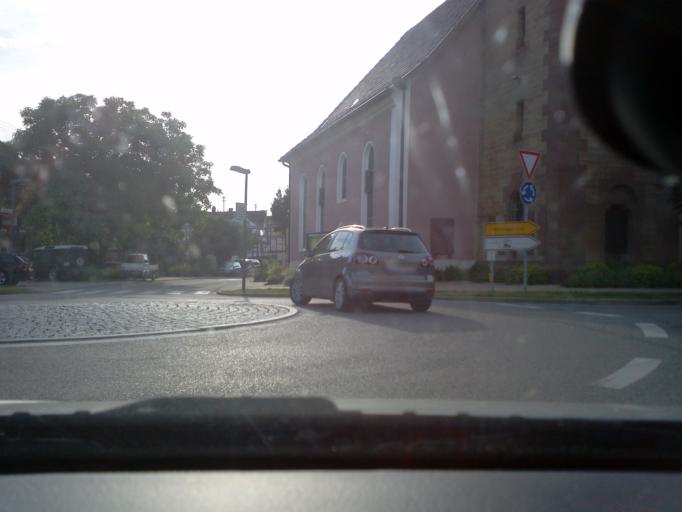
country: DE
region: Baden-Wuerttemberg
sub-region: Karlsruhe Region
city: Olbronn-Durrn
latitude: 48.9816
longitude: 8.7507
